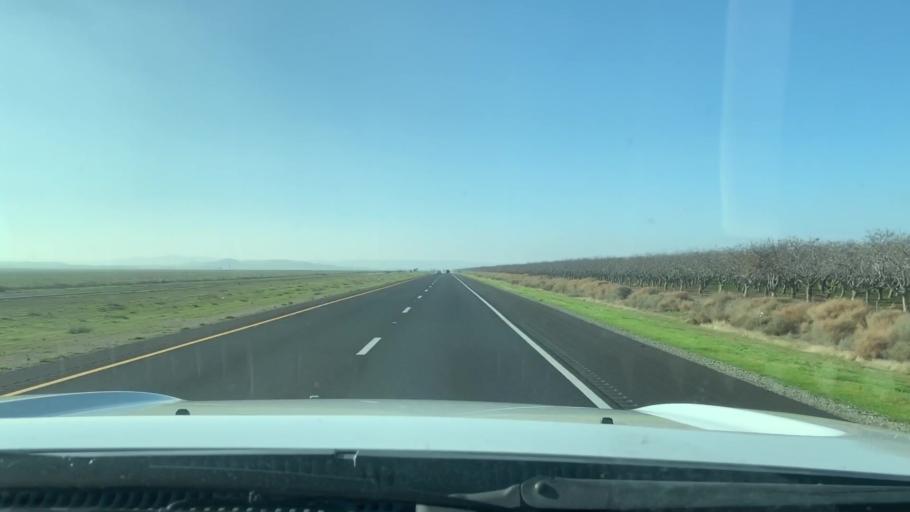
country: US
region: California
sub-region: Kern County
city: Lost Hills
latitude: 35.6148
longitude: -119.9141
